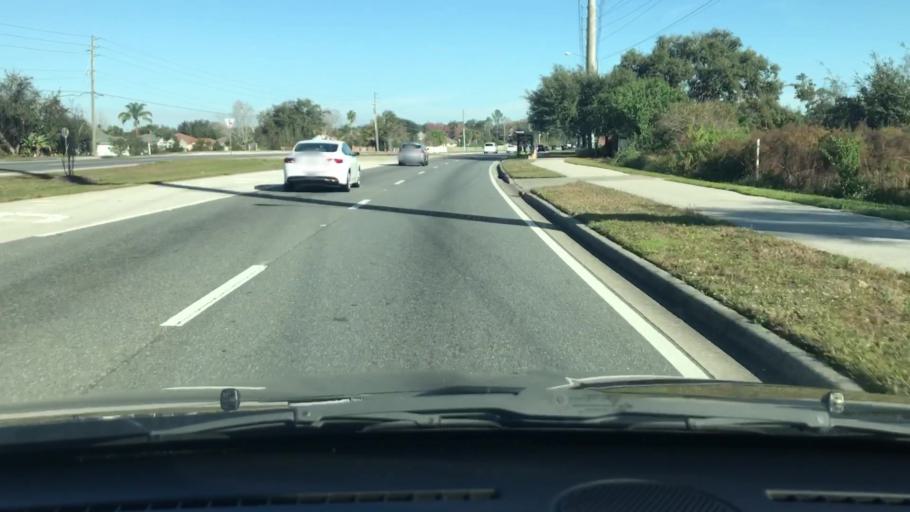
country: US
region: Florida
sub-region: Osceola County
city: Campbell
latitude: 28.2418
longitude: -81.4358
